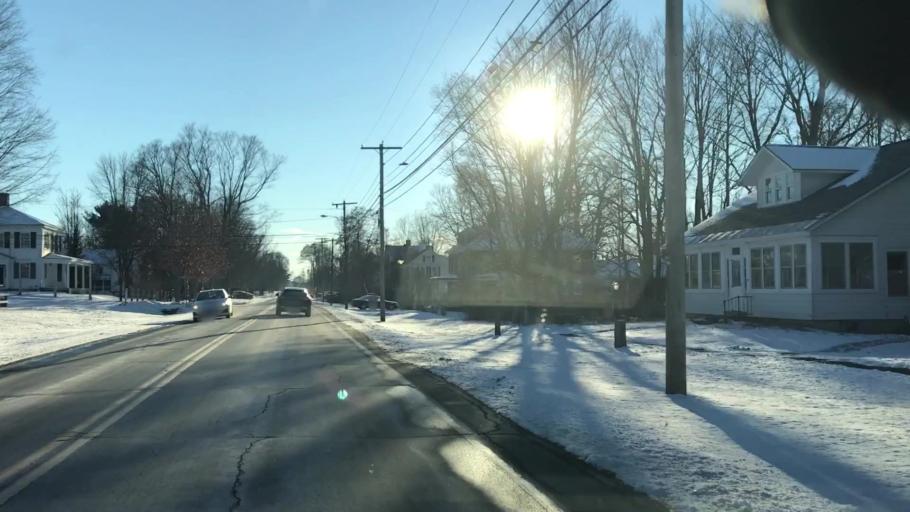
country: US
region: New Hampshire
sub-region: Grafton County
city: Haverhill
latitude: 44.0338
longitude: -72.0640
